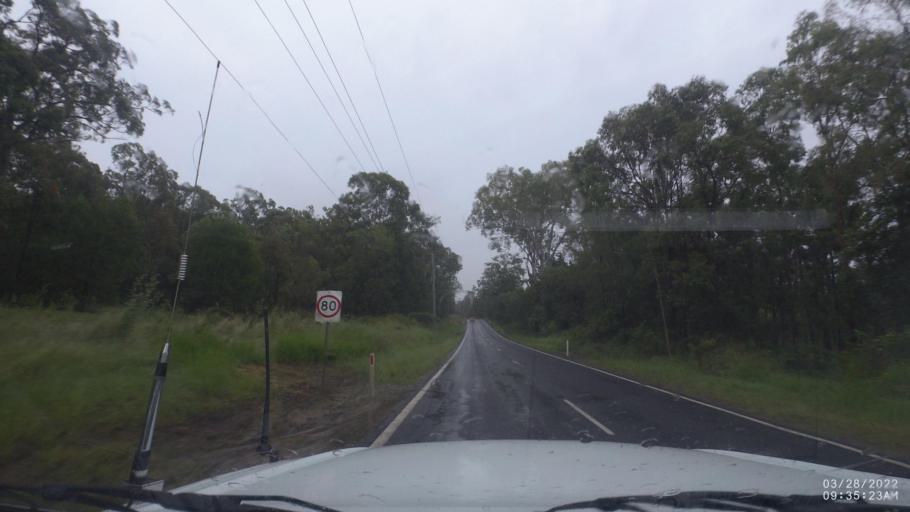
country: AU
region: Queensland
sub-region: Logan
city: Chambers Flat
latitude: -27.8308
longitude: 153.1059
